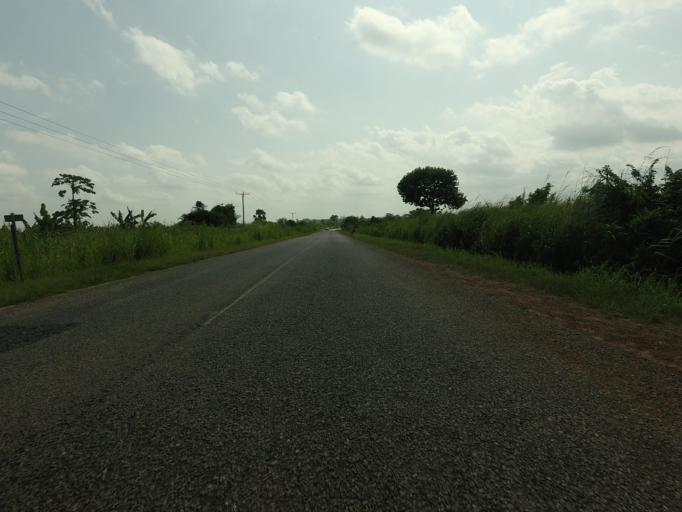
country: TG
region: Maritime
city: Tsevie
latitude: 6.3928
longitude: 0.8150
